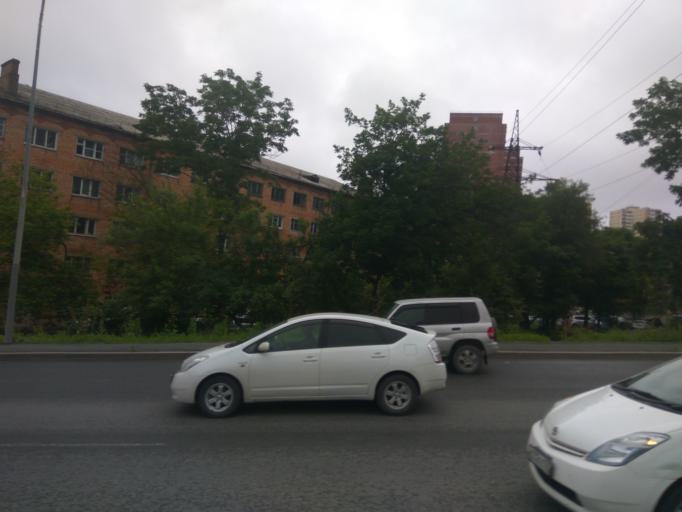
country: RU
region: Primorskiy
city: Vladivostok
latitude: 43.0930
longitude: 131.9115
